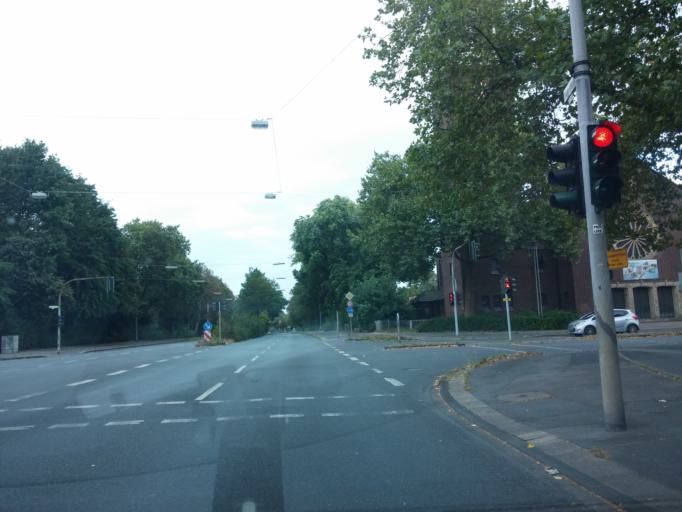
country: DE
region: North Rhine-Westphalia
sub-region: Regierungsbezirk Munster
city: Gelsenkirchen
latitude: 51.5188
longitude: 7.1269
